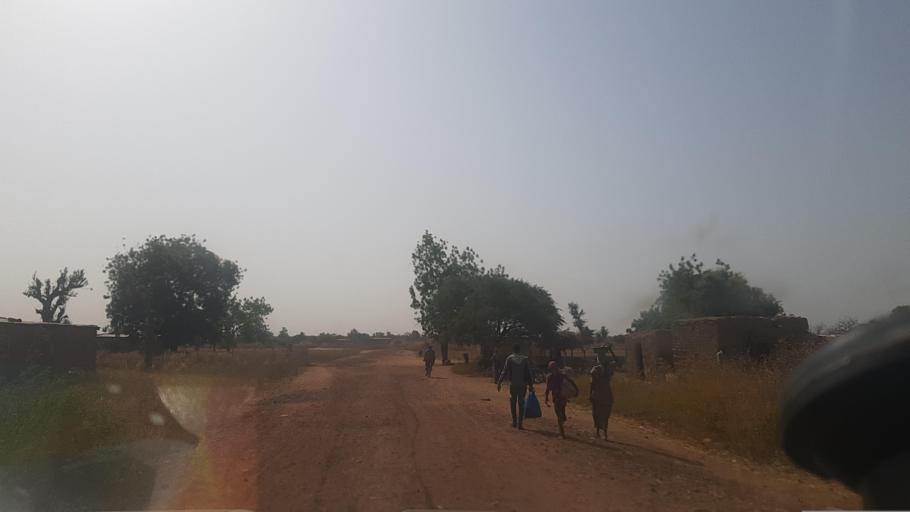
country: ML
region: Segou
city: Baroueli
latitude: 13.1643
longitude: -6.5182
